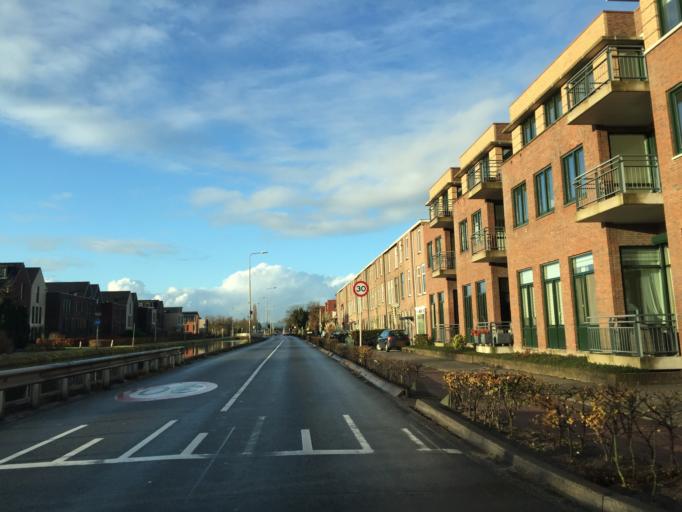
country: NL
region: South Holland
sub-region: Gemeente Delft
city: Delft
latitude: 52.0088
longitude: 4.3926
